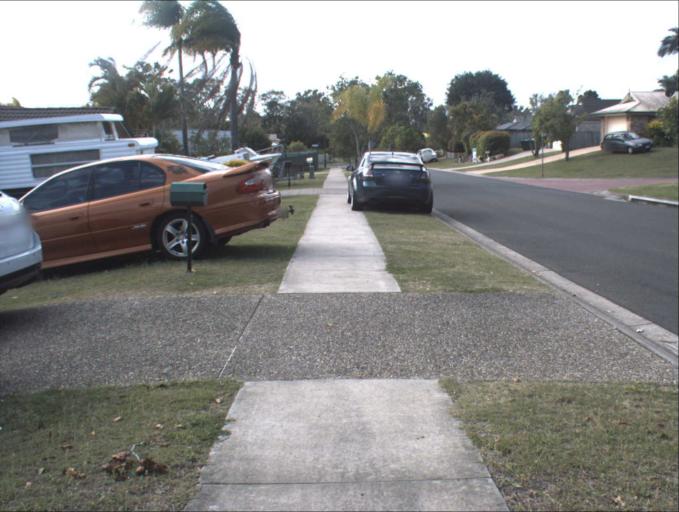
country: AU
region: Queensland
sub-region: Logan
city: Park Ridge South
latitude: -27.6891
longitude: 153.0513
